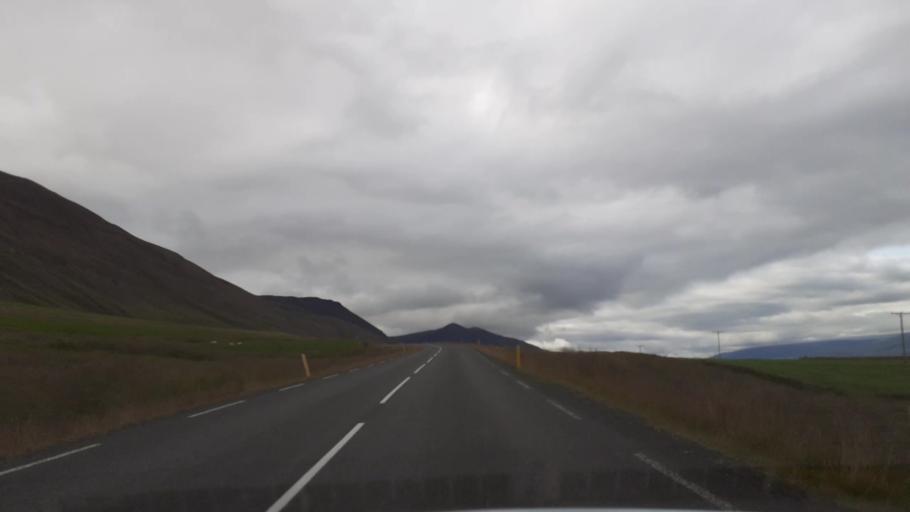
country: IS
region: Northeast
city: Akureyri
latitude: 65.8652
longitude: -18.0735
